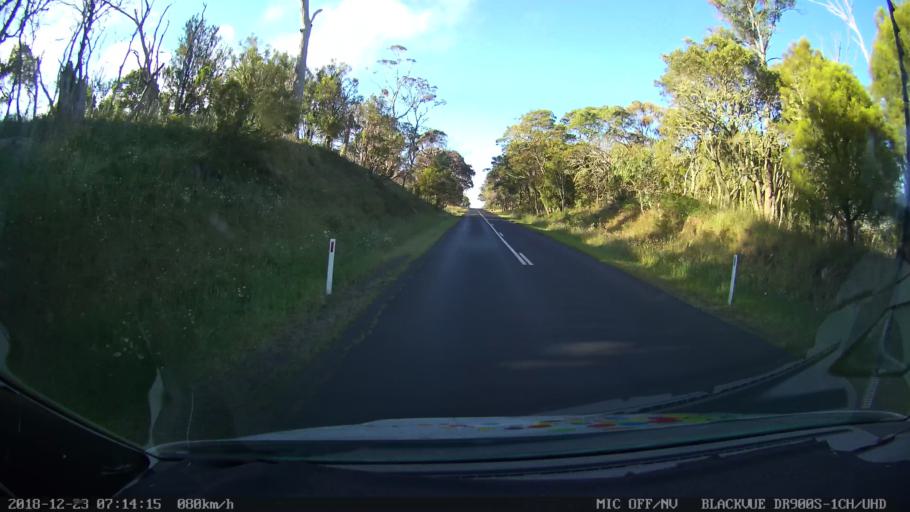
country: AU
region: New South Wales
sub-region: Bellingen
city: Dorrigo
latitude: -30.4331
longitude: 152.3236
